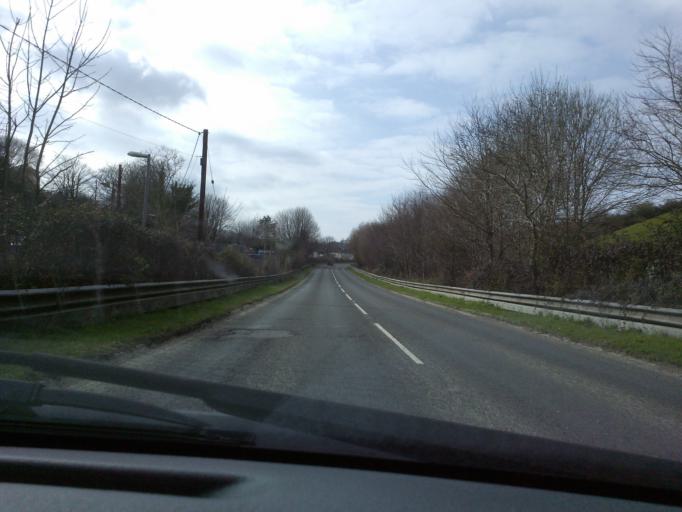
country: GB
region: England
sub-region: Cornwall
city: Penzance
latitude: 50.1278
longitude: -5.5340
